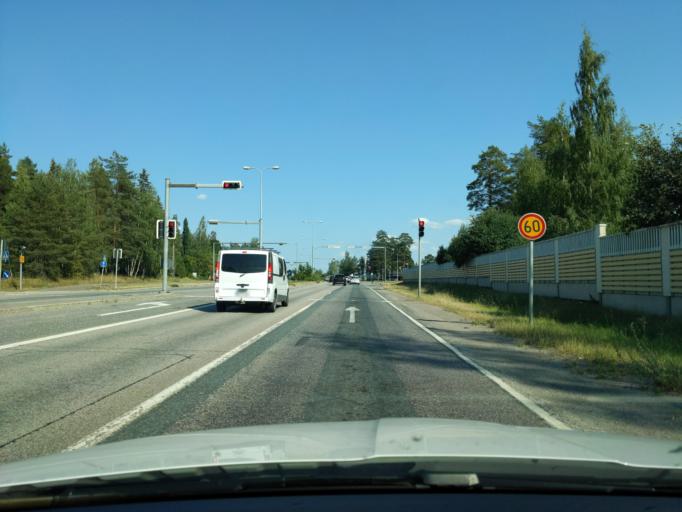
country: FI
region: Paijanne Tavastia
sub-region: Lahti
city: Lahti
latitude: 60.9795
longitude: 25.6070
